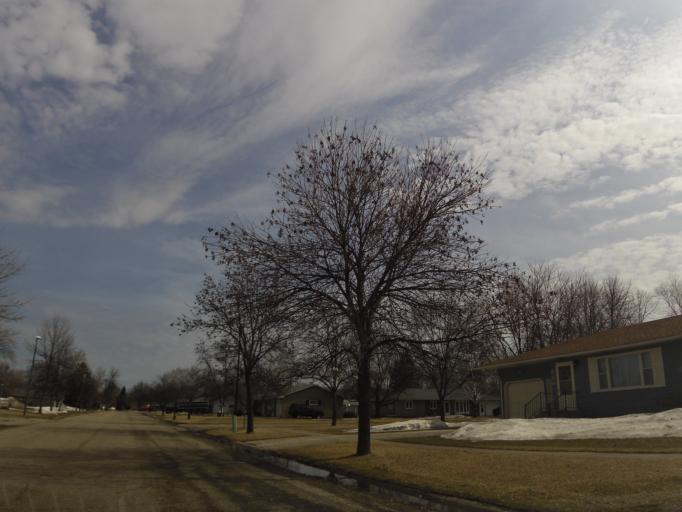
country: US
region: North Dakota
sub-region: Walsh County
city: Grafton
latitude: 48.4110
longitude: -97.4241
